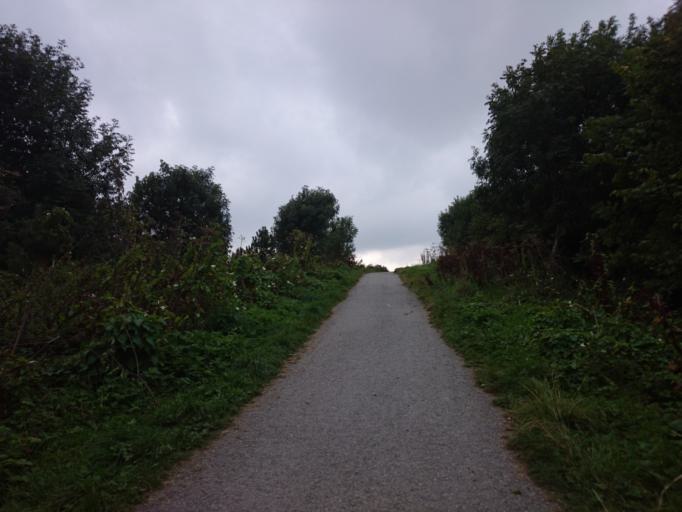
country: IE
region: Leinster
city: Shankill
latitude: 53.2287
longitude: -6.1125
